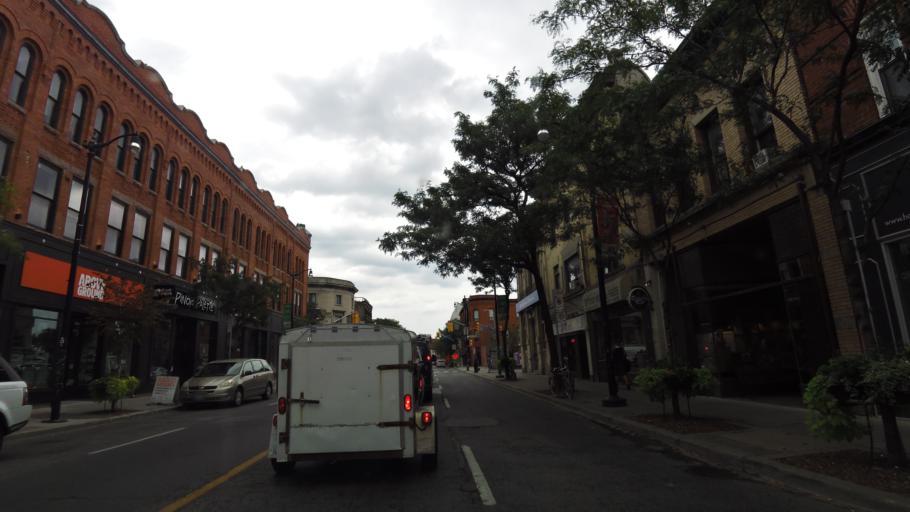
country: CA
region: Ontario
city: Toronto
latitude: 43.6654
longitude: -79.4654
